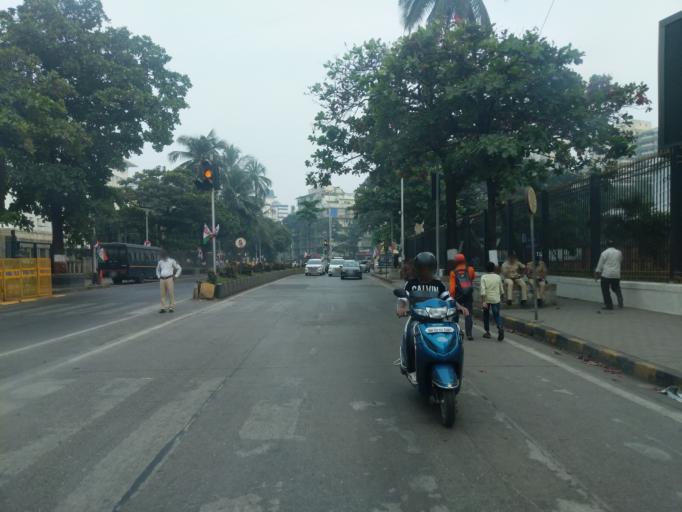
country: IN
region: Maharashtra
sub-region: Raigarh
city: Uran
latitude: 18.9270
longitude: 72.8261
